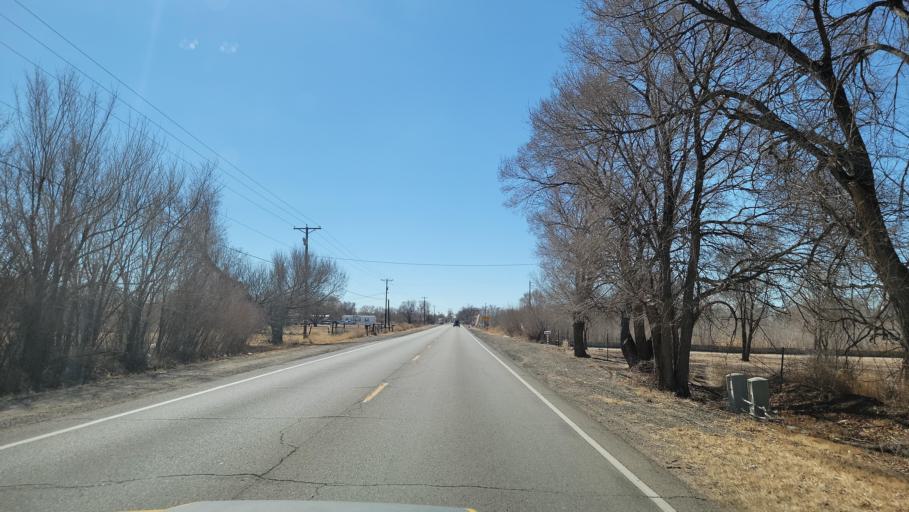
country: US
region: New Mexico
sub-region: Valencia County
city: Bosque Farms
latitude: 34.9277
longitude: -106.6928
